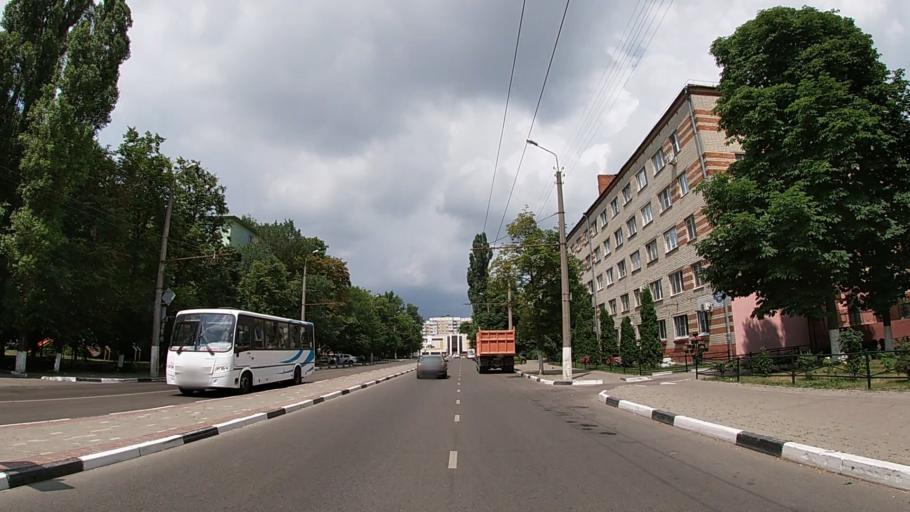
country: RU
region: Belgorod
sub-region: Belgorodskiy Rayon
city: Belgorod
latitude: 50.6112
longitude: 36.5915
